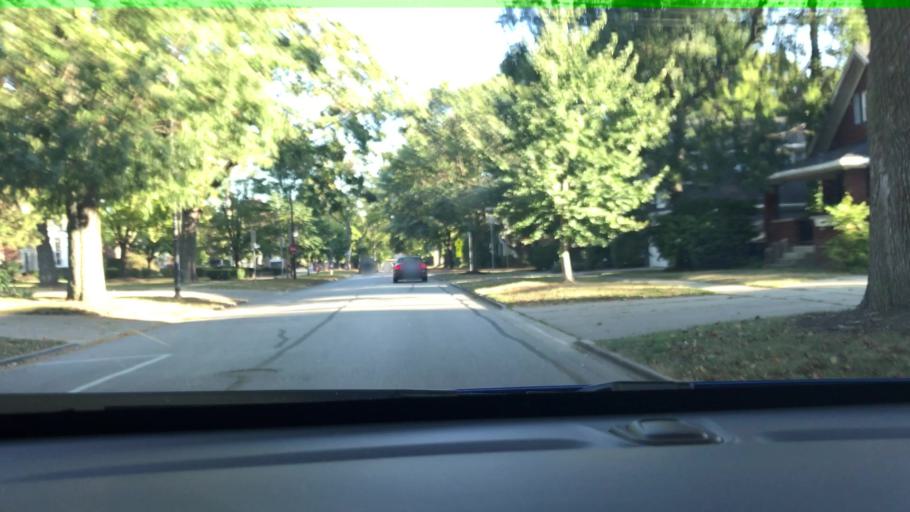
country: US
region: Illinois
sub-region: DuPage County
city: Naperville
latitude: 41.7735
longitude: -88.1529
